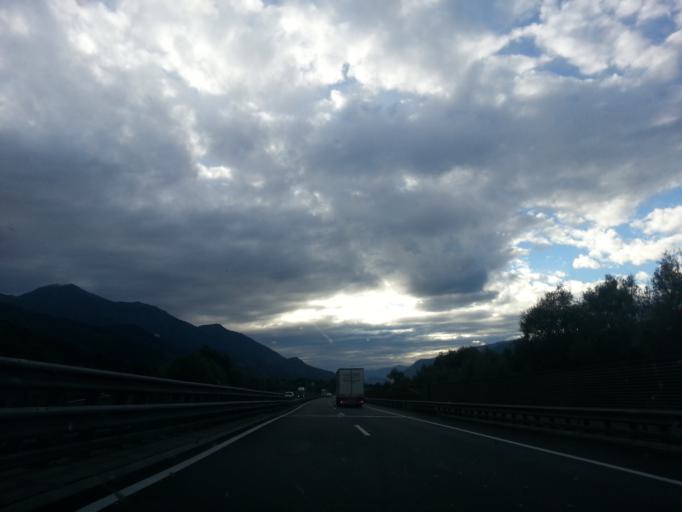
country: AT
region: Styria
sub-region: Politischer Bezirk Liezen
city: Trieben
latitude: 47.4869
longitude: 14.5224
